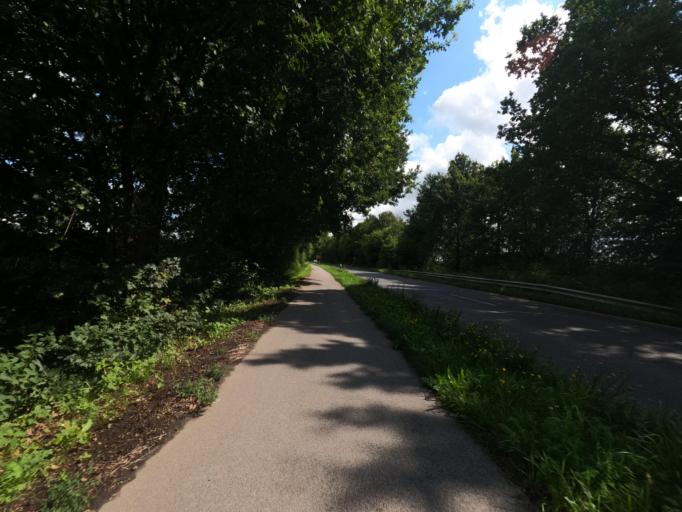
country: DE
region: North Rhine-Westphalia
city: Baesweiler
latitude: 50.9146
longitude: 6.1617
